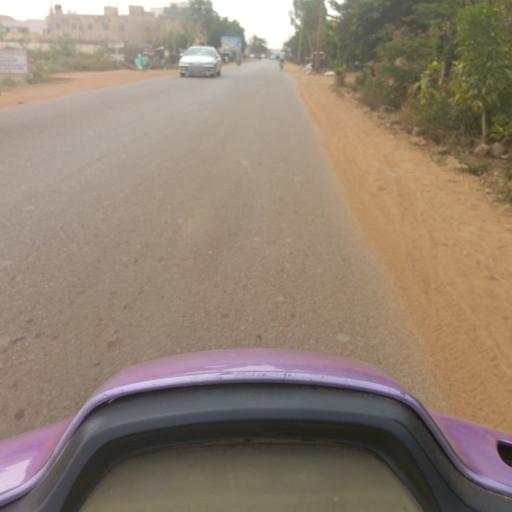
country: ML
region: Bamako
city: Bamako
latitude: 12.6589
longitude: -7.9361
